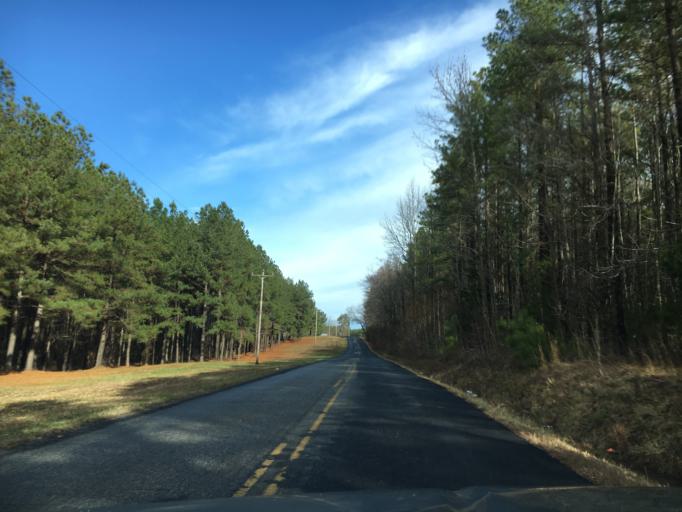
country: US
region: Virginia
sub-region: Nottoway County
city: Crewe
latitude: 37.2900
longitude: -78.2001
